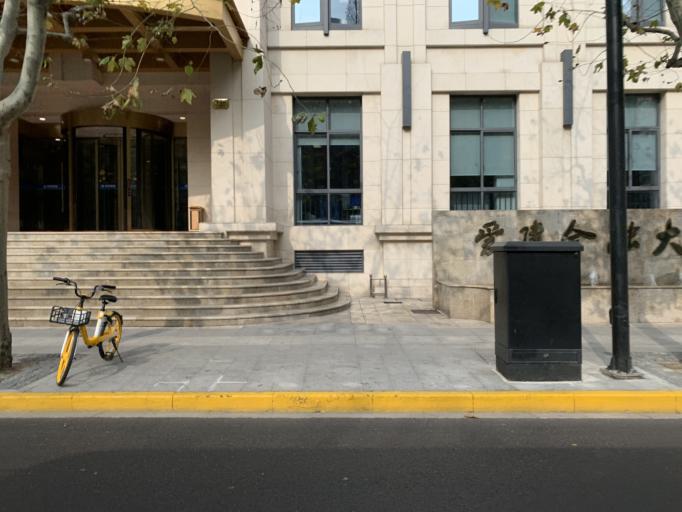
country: CN
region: Shanghai Shi
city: Xuhui
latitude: 31.2005
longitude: 121.4422
